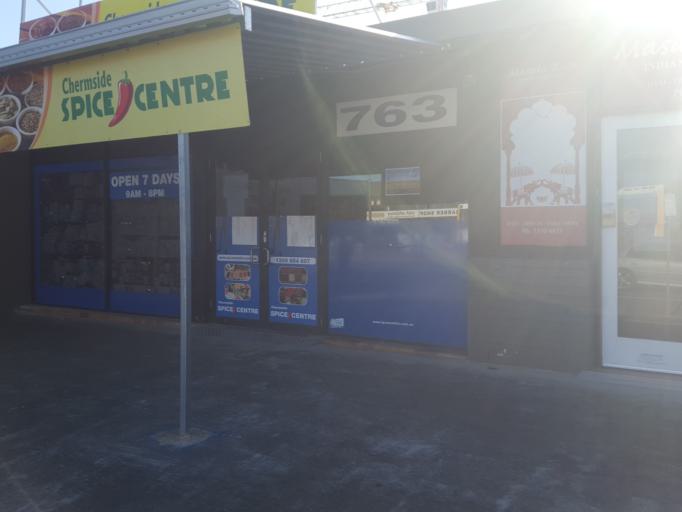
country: AU
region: Queensland
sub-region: Brisbane
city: Chermside West
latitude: -27.3886
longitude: 153.0314
